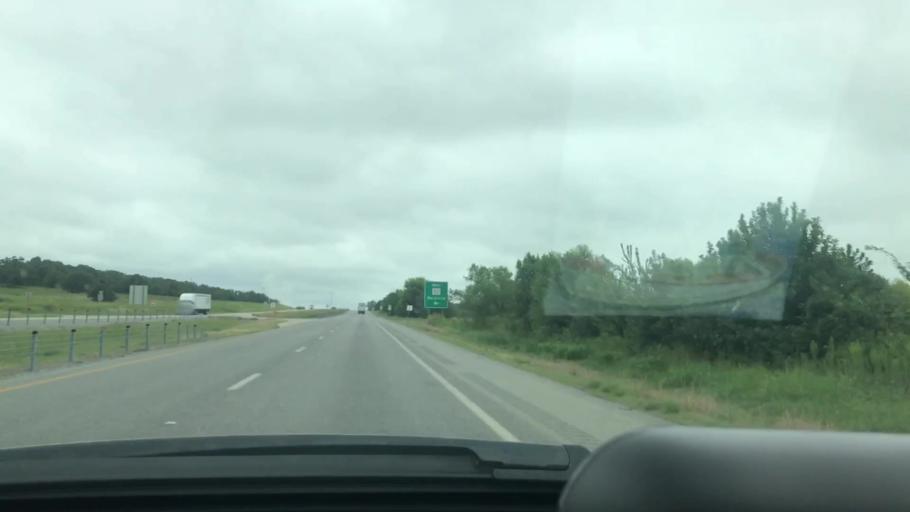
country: US
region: Oklahoma
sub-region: Coal County
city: Coalgate
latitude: 34.6648
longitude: -95.9382
